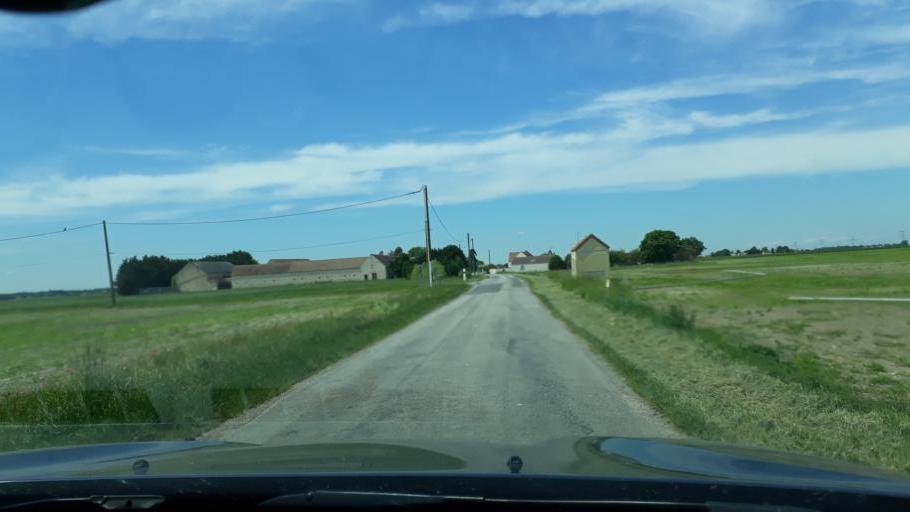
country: FR
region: Centre
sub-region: Departement du Loiret
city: Dadonville
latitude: 48.1022
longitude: 2.2651
